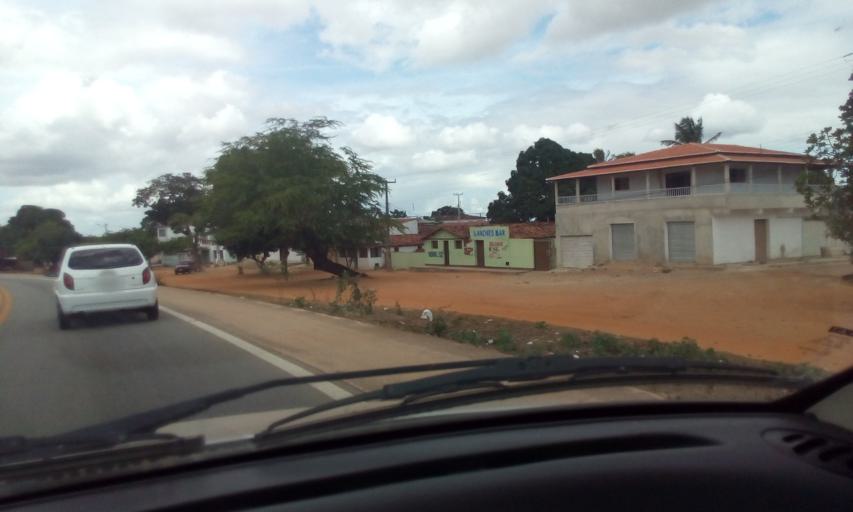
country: BR
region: Rio Grande do Norte
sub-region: Macaiba
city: Macaiba
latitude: -5.9261
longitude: -35.5383
